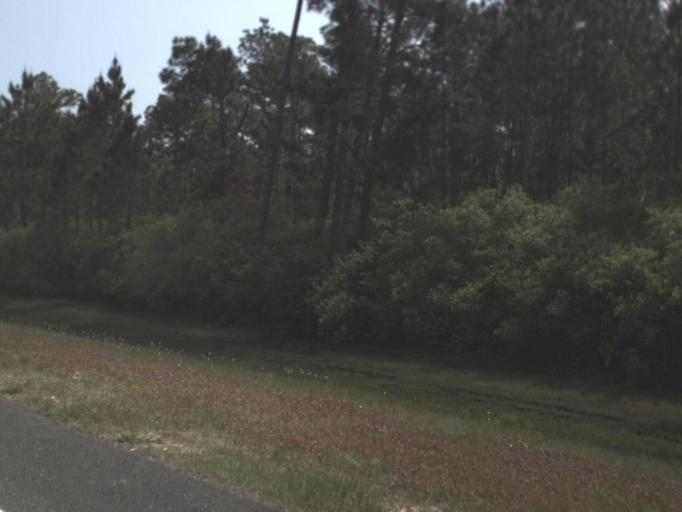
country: US
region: Florida
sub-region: Santa Rosa County
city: Bagdad
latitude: 30.5108
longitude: -87.0838
